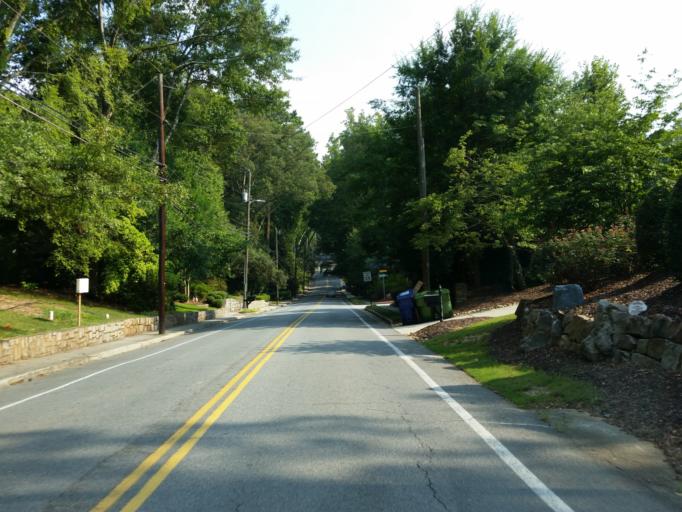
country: US
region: Georgia
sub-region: DeKalb County
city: North Atlanta
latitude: 33.8665
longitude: -84.3579
